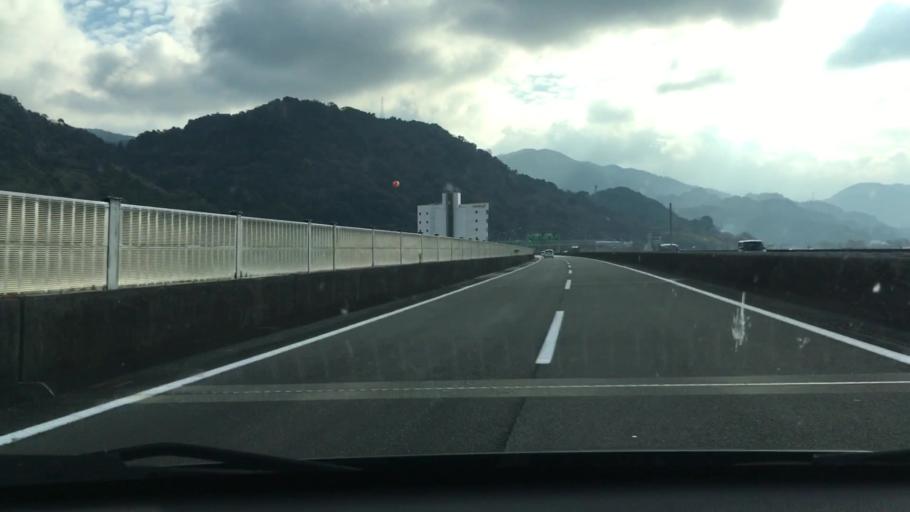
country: JP
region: Kumamoto
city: Yatsushiro
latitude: 32.5097
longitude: 130.6468
